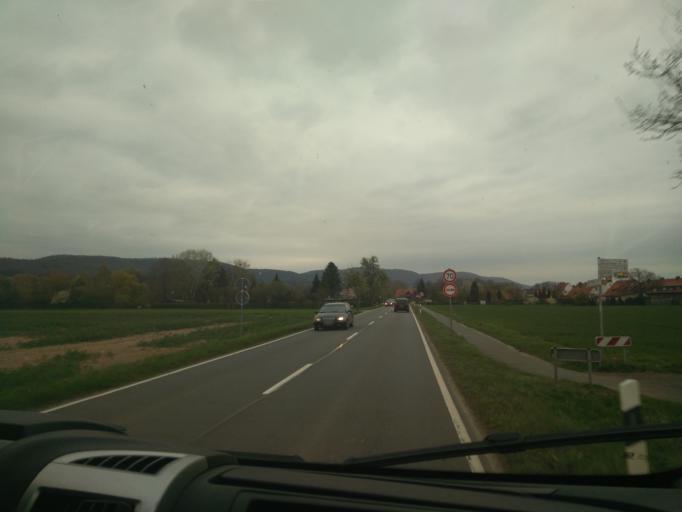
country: DE
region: Lower Saxony
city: Buchholz
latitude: 52.1942
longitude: 9.1242
